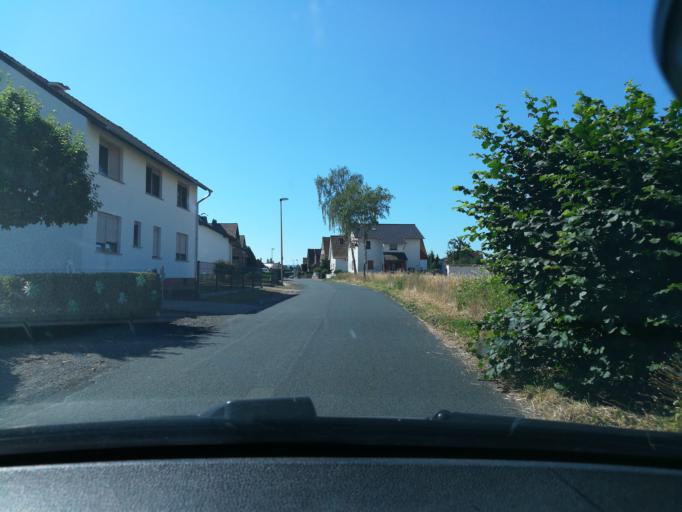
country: DE
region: North Rhine-Westphalia
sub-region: Regierungsbezirk Detmold
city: Minden
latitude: 52.3116
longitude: 8.9287
